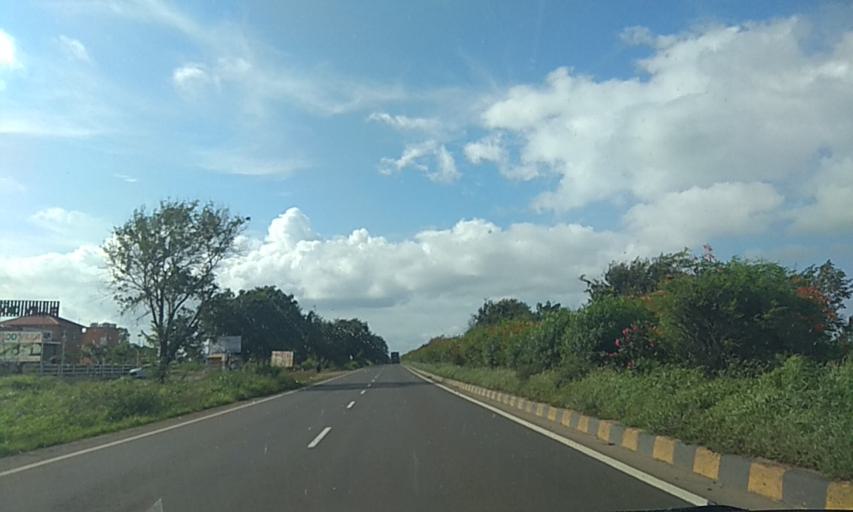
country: IN
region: Maharashtra
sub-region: Kolhapur
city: Kodoli
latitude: 17.0229
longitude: 74.2507
